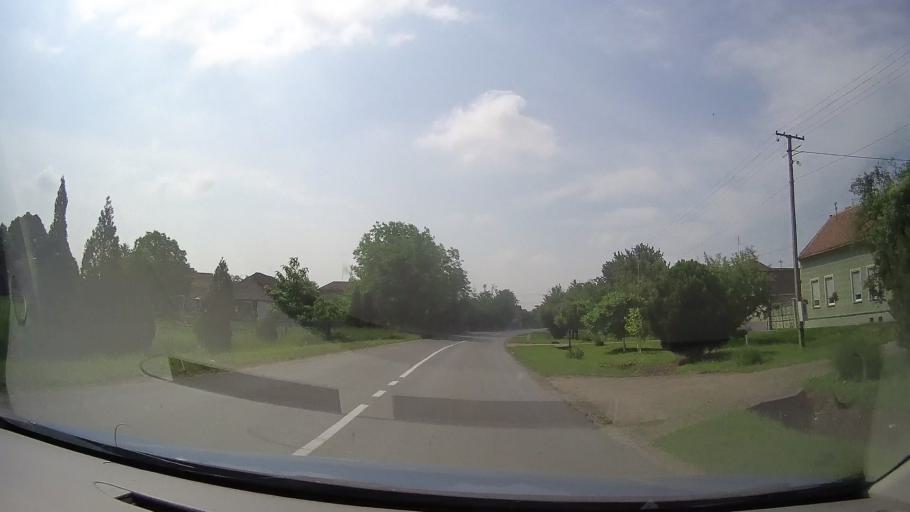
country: RS
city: Padina
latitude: 45.1269
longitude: 20.7215
